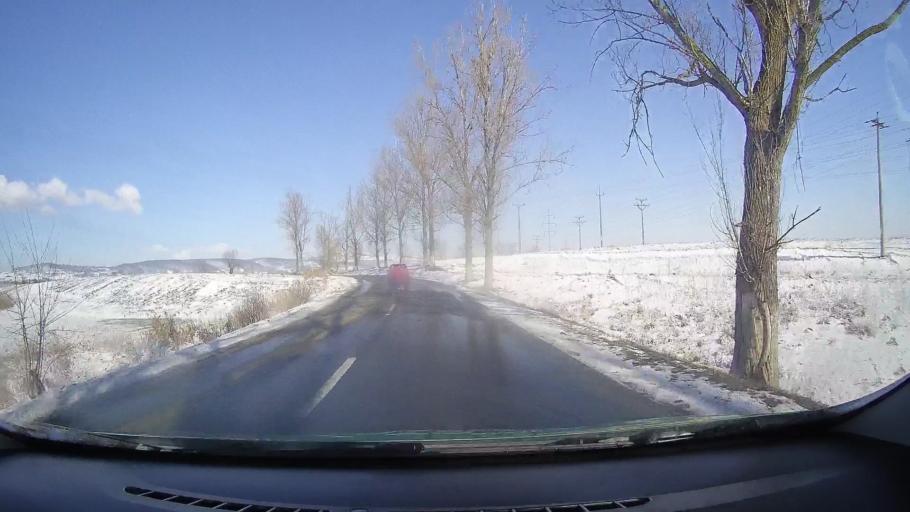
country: RO
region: Sibiu
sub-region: Comuna Avrig
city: Marsa
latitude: 45.7082
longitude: 24.3694
